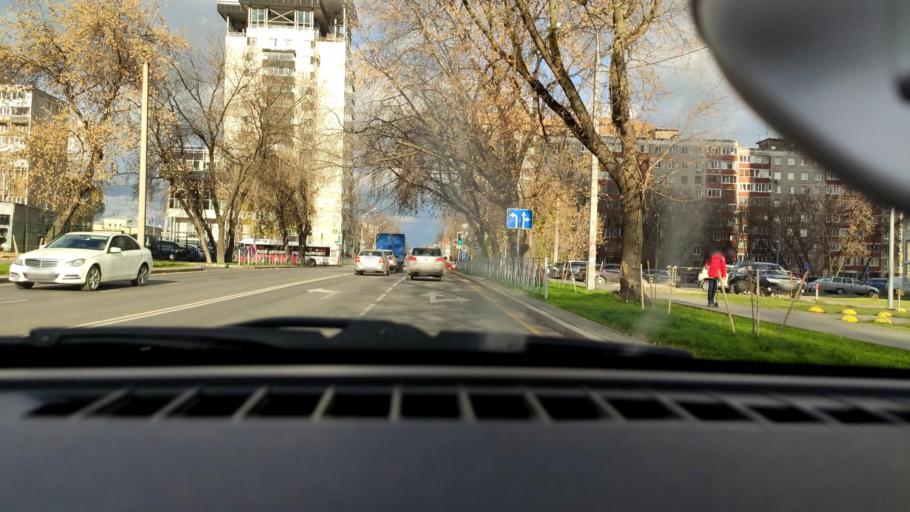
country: RU
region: Perm
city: Perm
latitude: 58.0104
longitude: 56.2614
